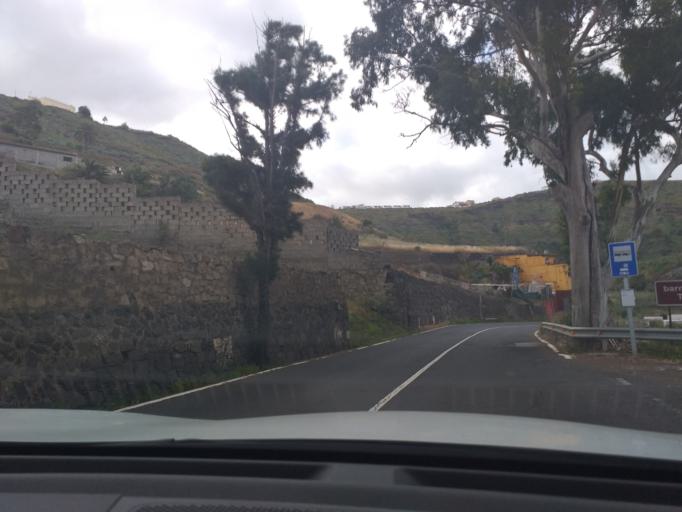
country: ES
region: Canary Islands
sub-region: Provincia de Las Palmas
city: Arucas
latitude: 28.1099
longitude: -15.4994
